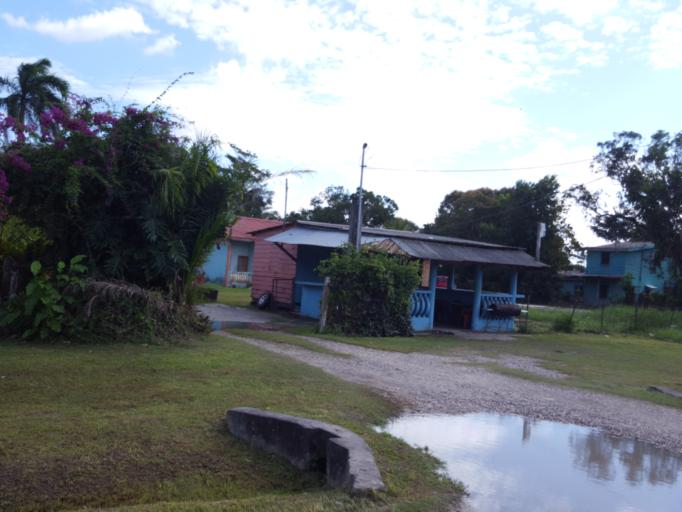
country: BZ
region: Belize
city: Belize City
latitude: 17.5674
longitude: -88.4056
